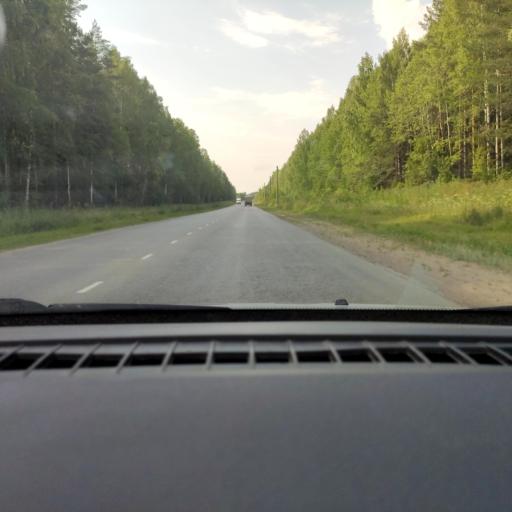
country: RU
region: Perm
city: Overyata
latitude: 58.0126
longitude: 55.8681
